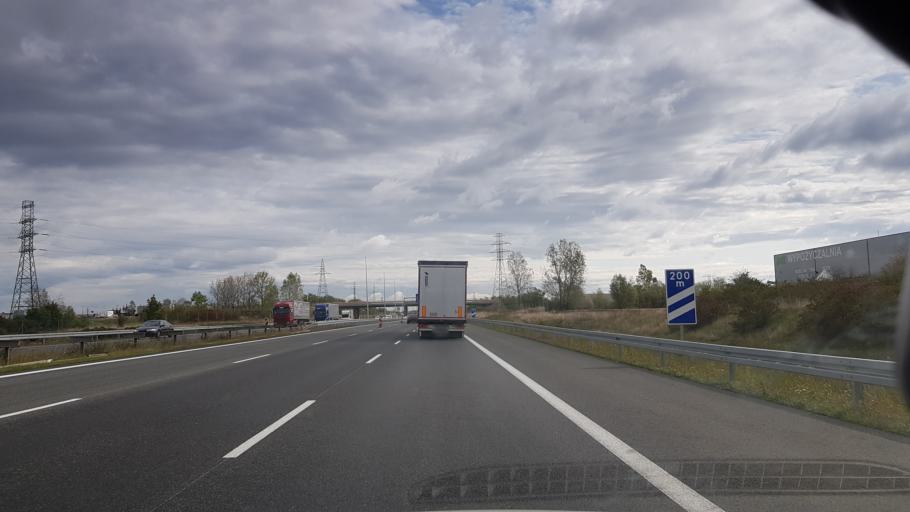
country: PL
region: Greater Poland Voivodeship
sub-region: Powiat poznanski
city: Komorniki
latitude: 52.3502
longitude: 16.8195
